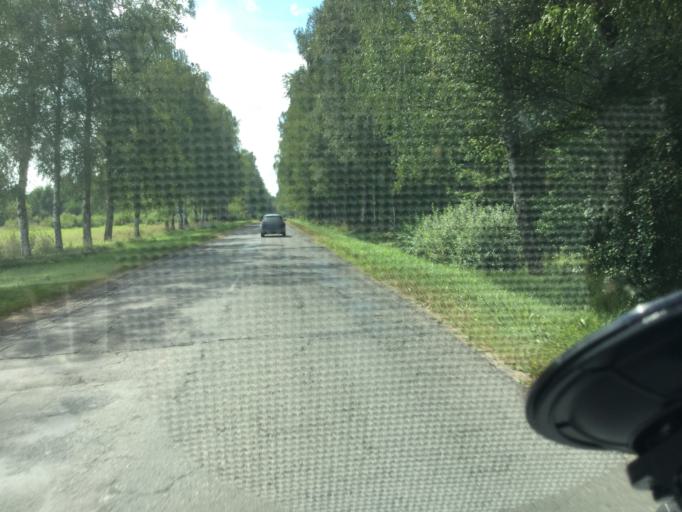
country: BY
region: Vitebsk
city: Chashniki
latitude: 55.3051
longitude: 29.3977
